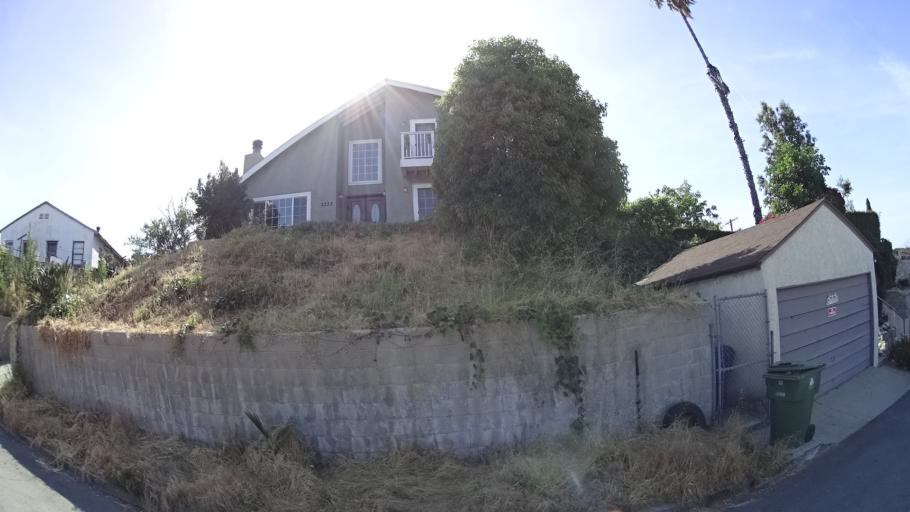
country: US
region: California
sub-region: Los Angeles County
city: Belvedere
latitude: 34.0732
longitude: -118.1672
